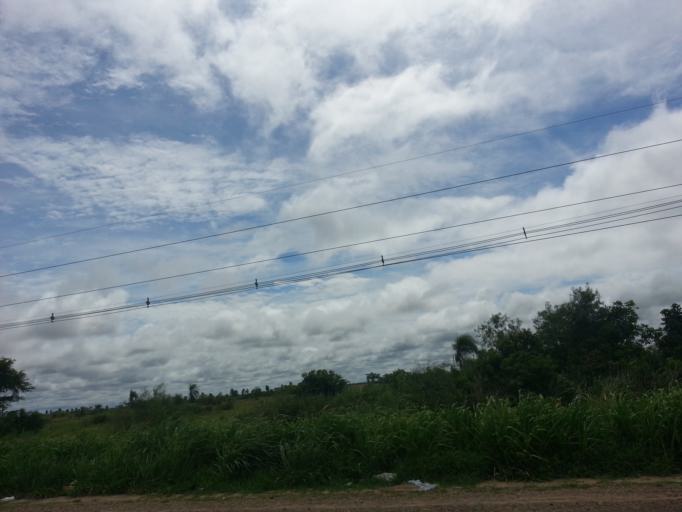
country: BO
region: Santa Cruz
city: La Belgica
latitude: -17.6345
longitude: -63.1580
